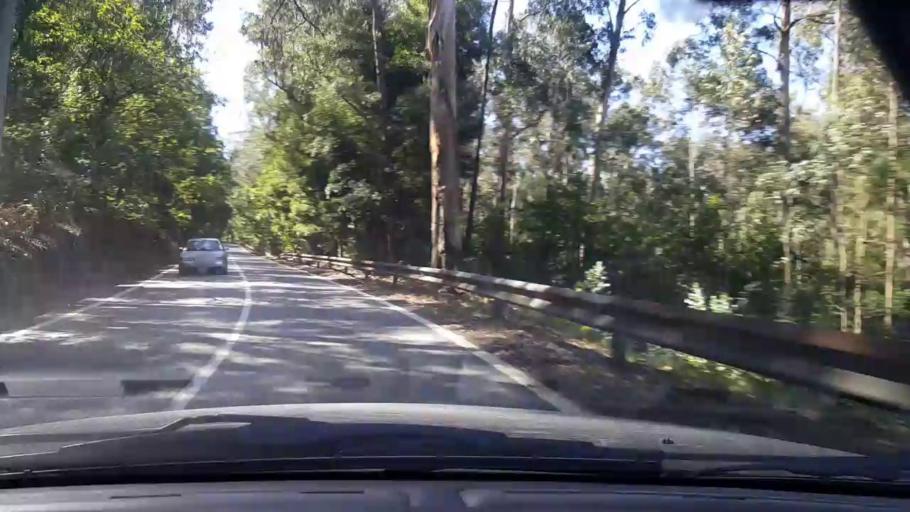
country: PT
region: Braga
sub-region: Vila Nova de Famalicao
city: Ribeirao
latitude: 41.3404
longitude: -8.6260
